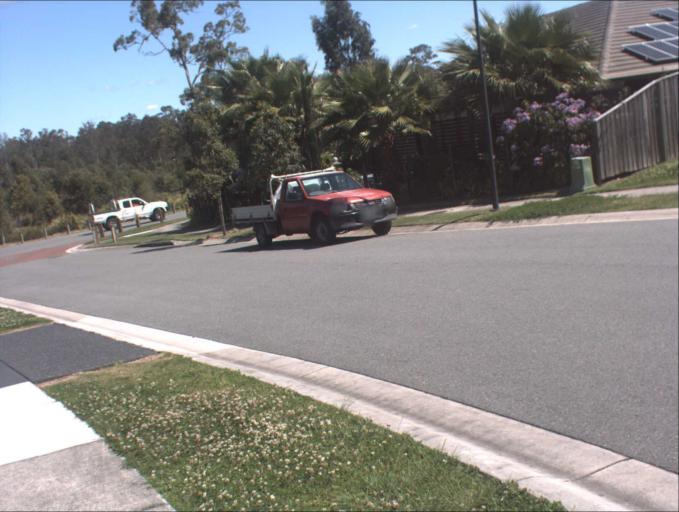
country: AU
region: Queensland
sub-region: Logan
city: Waterford West
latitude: -27.7149
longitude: 153.1484
